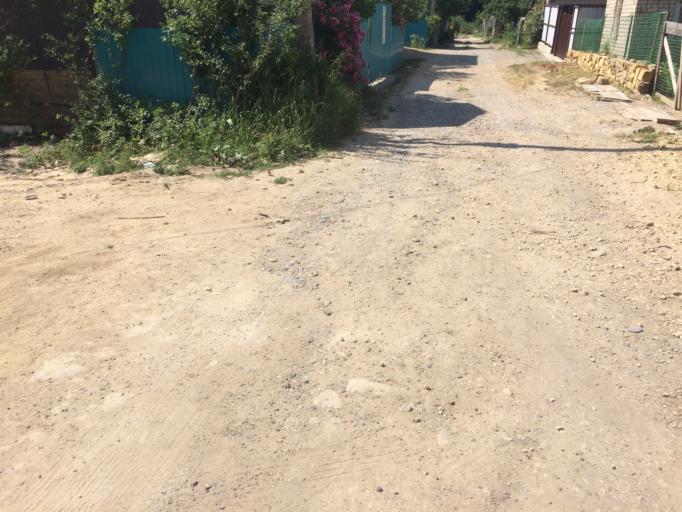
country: RU
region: Stavropol'skiy
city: Tatarka
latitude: 44.9811
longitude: 41.9408
